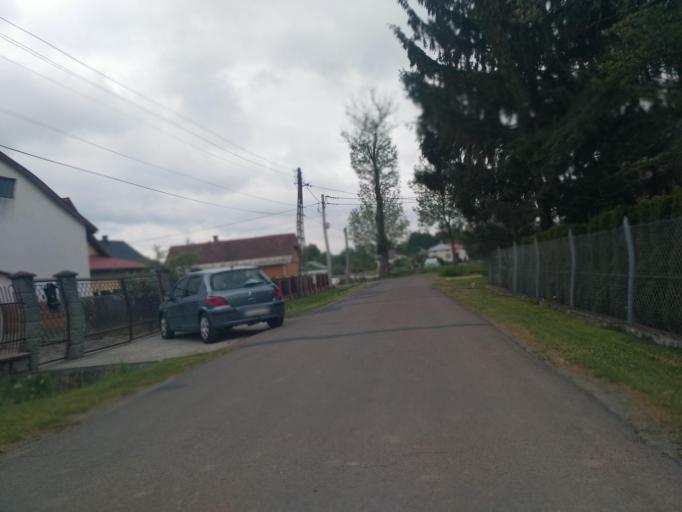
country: PL
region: Subcarpathian Voivodeship
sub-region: Powiat krosnienski
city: Chorkowka
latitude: 49.6675
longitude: 21.7034
